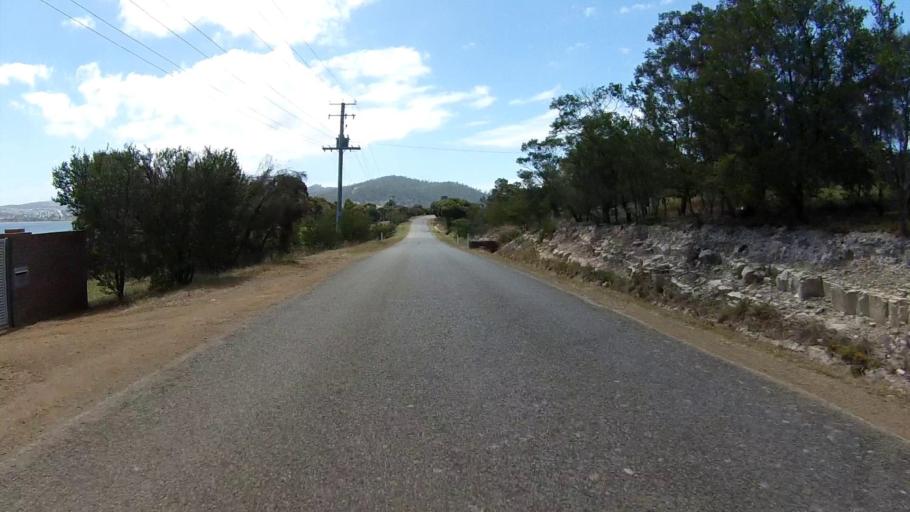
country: AU
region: Tasmania
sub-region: Clarence
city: Lauderdale
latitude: -42.9274
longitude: 147.4658
